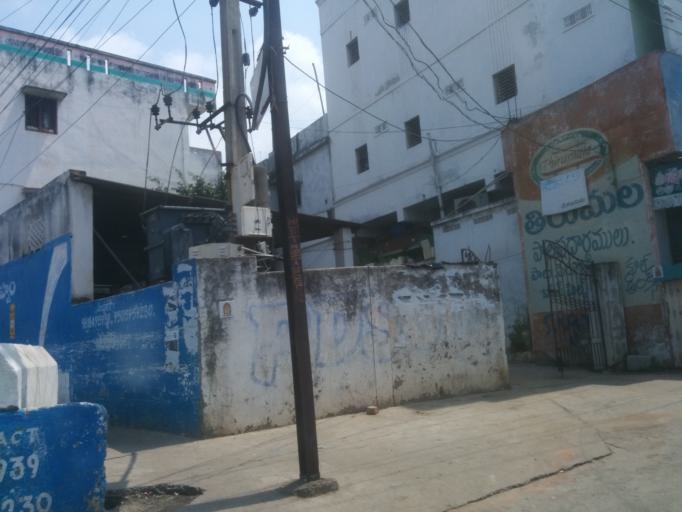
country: IN
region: Andhra Pradesh
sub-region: East Godavari
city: Rajahmundry
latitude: 17.0146
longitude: 81.7764
